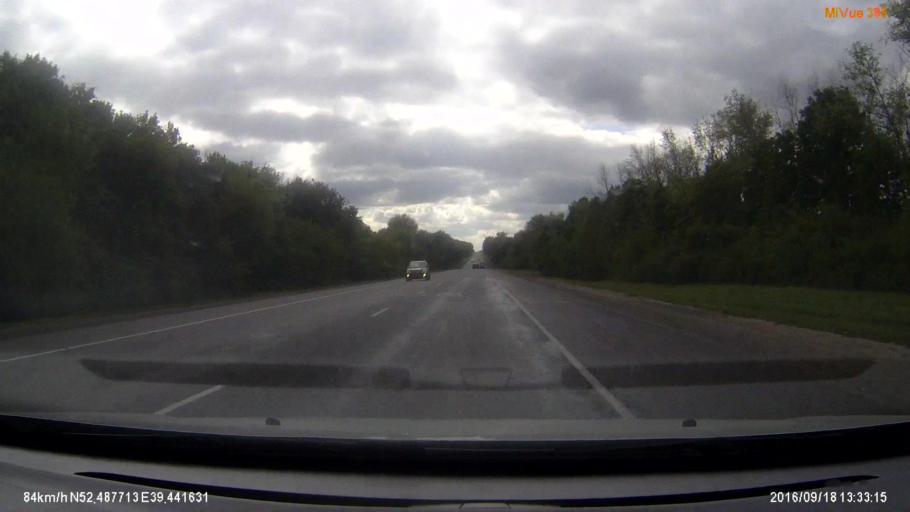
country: RU
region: Lipetsk
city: Borinskoye
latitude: 52.4760
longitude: 39.4270
